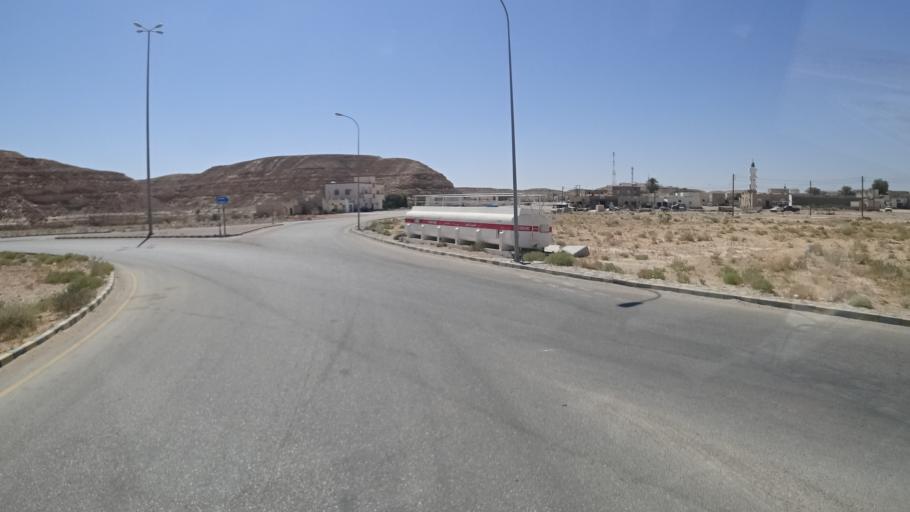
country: OM
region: Zufar
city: Salalah
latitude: 17.4882
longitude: 53.3529
